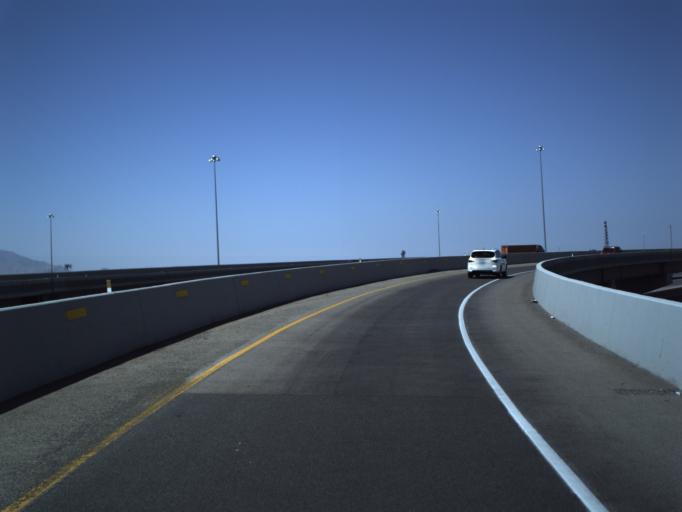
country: US
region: Utah
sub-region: Salt Lake County
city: South Salt Lake
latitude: 40.7188
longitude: -111.9014
